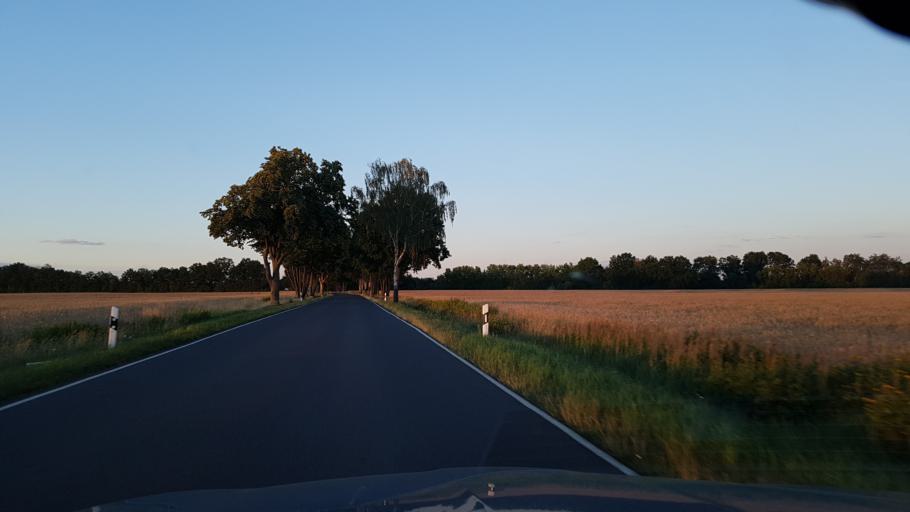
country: DE
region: Brandenburg
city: Plessa
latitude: 51.4272
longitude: 13.6119
